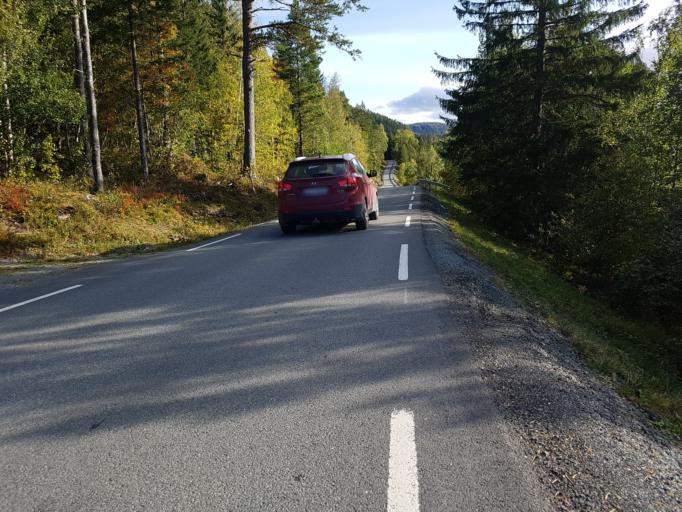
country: NO
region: Sor-Trondelag
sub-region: Malvik
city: Malvik
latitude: 63.3601
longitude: 10.6313
